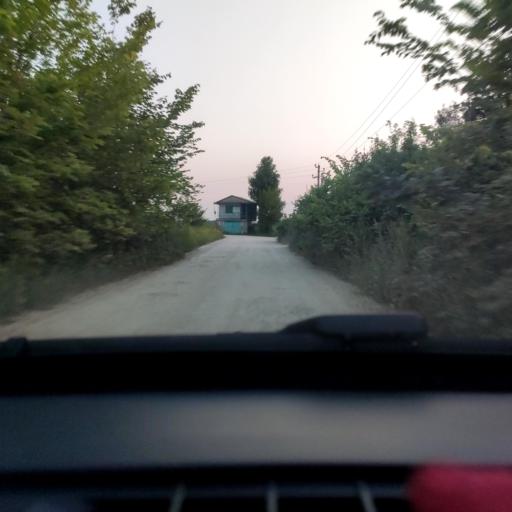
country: RU
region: Voronezj
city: Podgornoye
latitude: 51.8612
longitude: 39.1066
